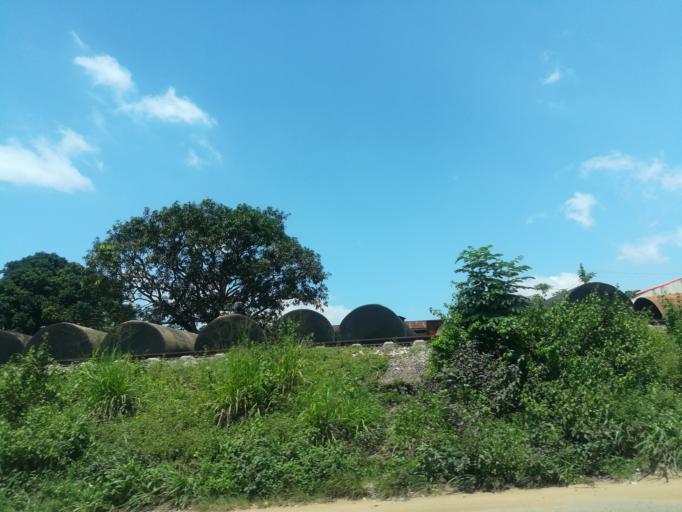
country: NG
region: Oyo
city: Ibadan
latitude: 7.3818
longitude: 3.8687
